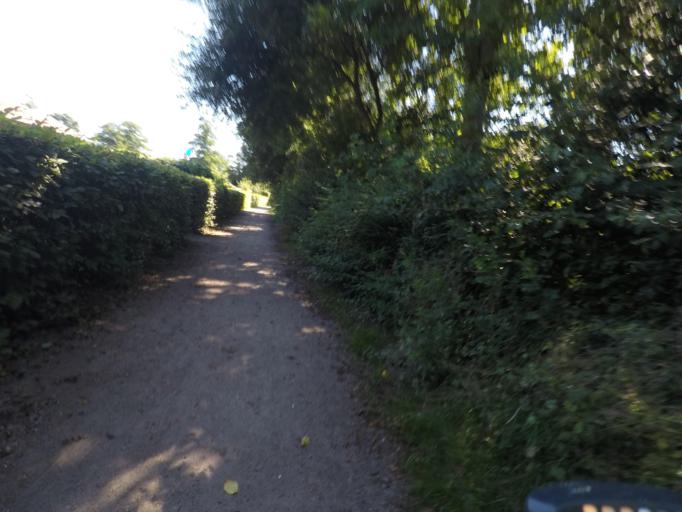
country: DE
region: Schleswig-Holstein
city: Barsbuettel
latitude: 53.5739
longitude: 10.1521
